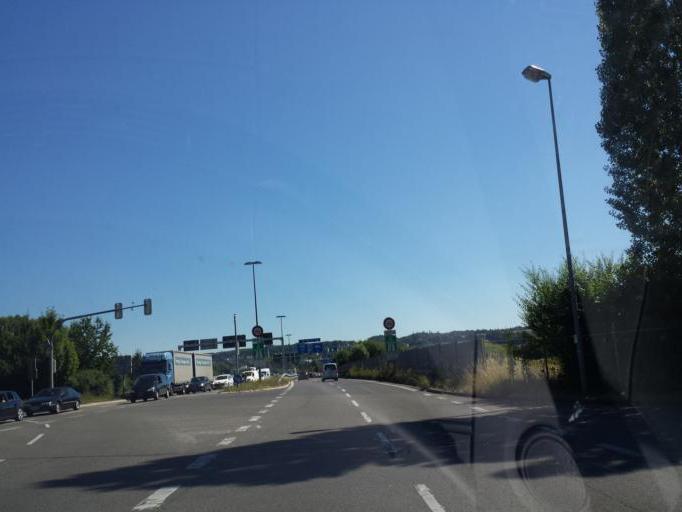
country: DE
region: Baden-Wuerttemberg
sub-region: Freiburg Region
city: Konstanz
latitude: 47.6621
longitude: 9.1613
